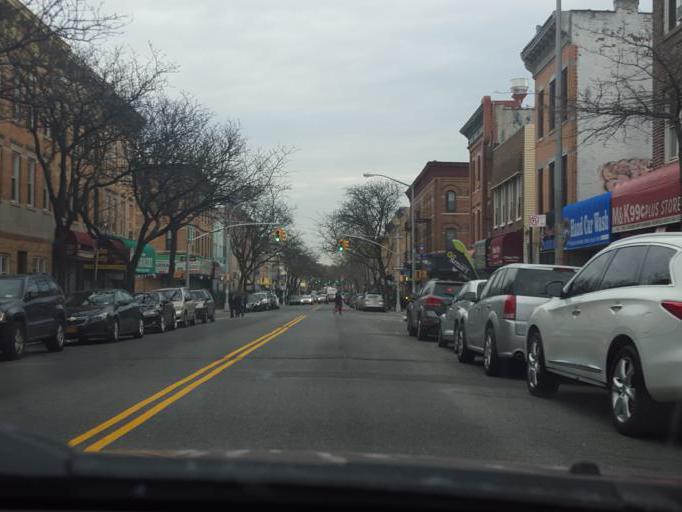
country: US
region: New York
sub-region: Kings County
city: East New York
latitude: 40.7023
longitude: -73.9068
